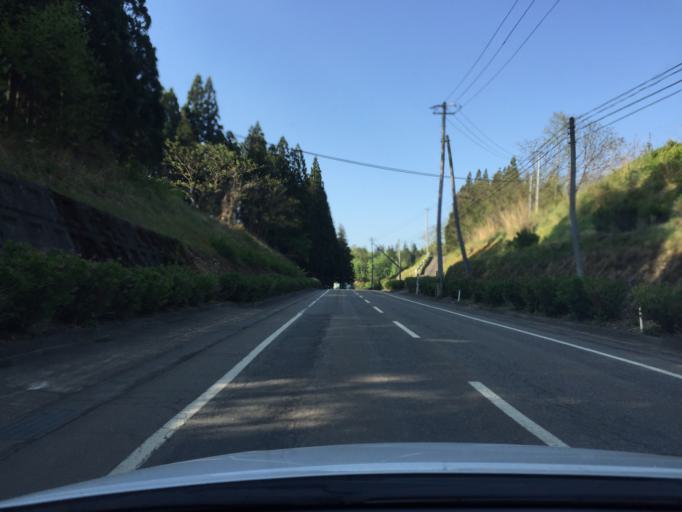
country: JP
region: Fukushima
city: Kitakata
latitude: 37.6775
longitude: 139.7915
